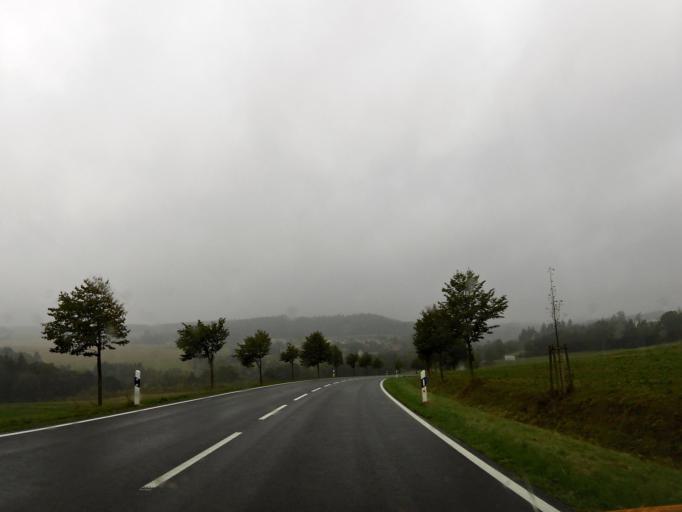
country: DE
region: Saxony-Anhalt
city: Friedrichsbrunn
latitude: 51.6473
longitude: 10.9976
